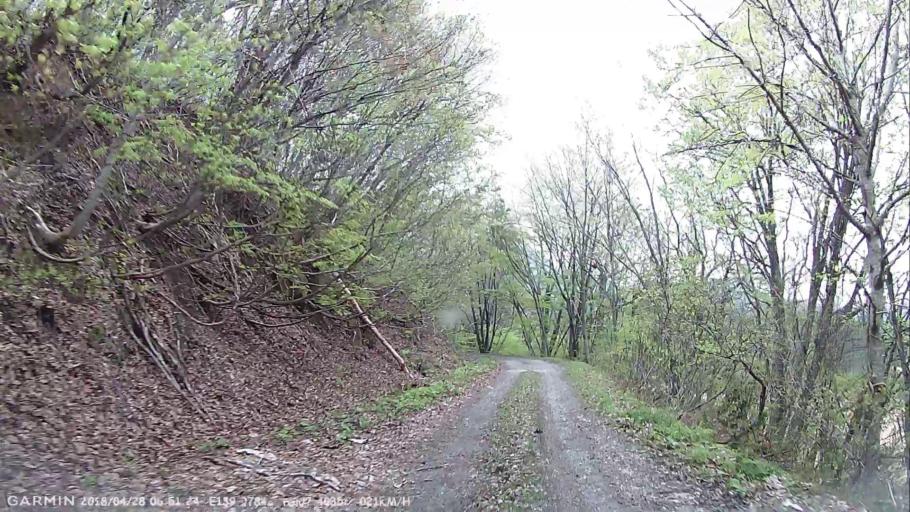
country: JP
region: Fukushima
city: Inawashiro
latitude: 37.4035
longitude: 139.9784
